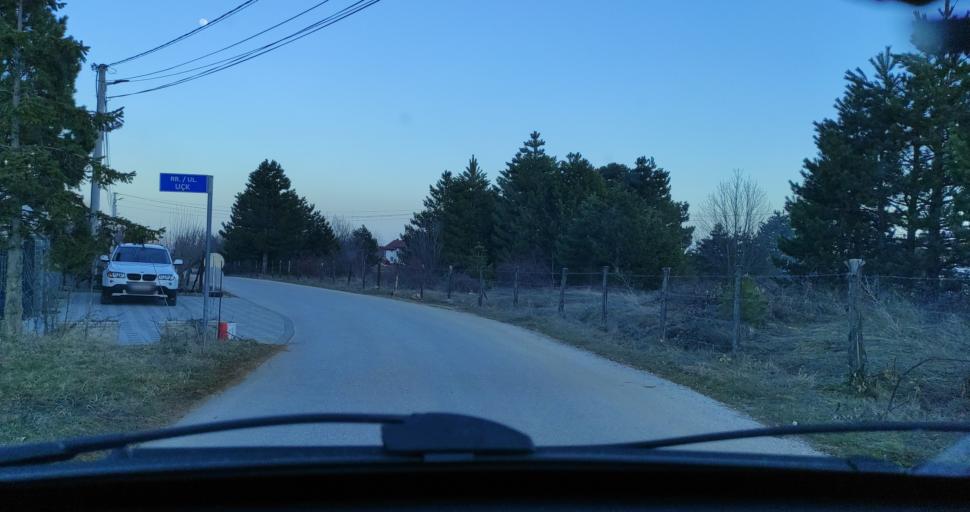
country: XK
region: Gjakova
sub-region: Komuna e Decanit
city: Decan
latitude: 42.5394
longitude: 20.2802
